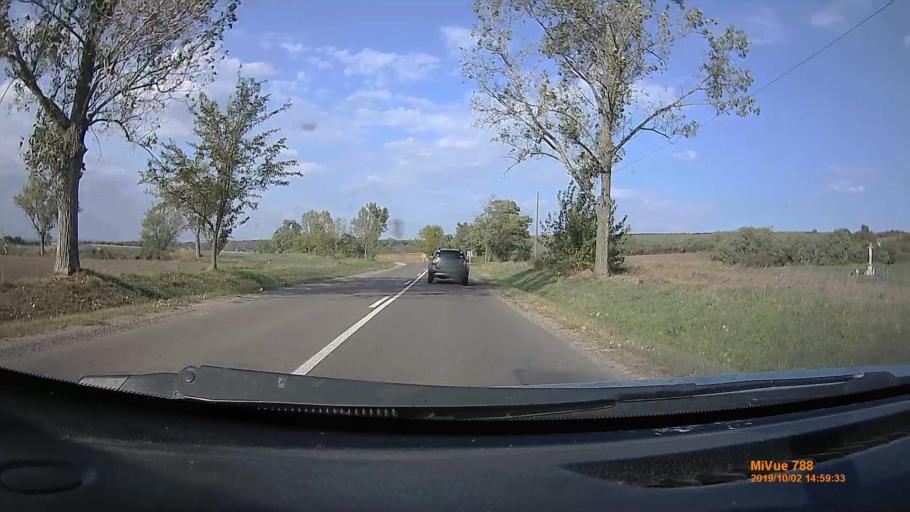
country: HU
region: Heves
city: Andornaktalya
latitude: 47.8259
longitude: 20.4193
